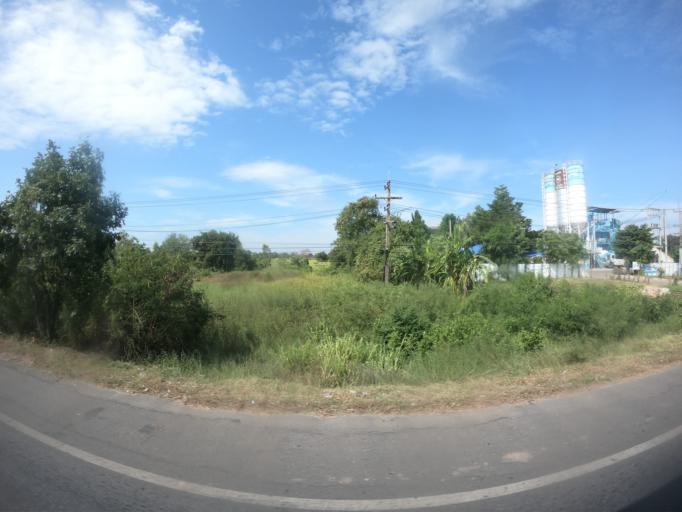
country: TH
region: Khon Kaen
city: Khon Kaen
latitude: 16.4325
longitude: 102.9175
